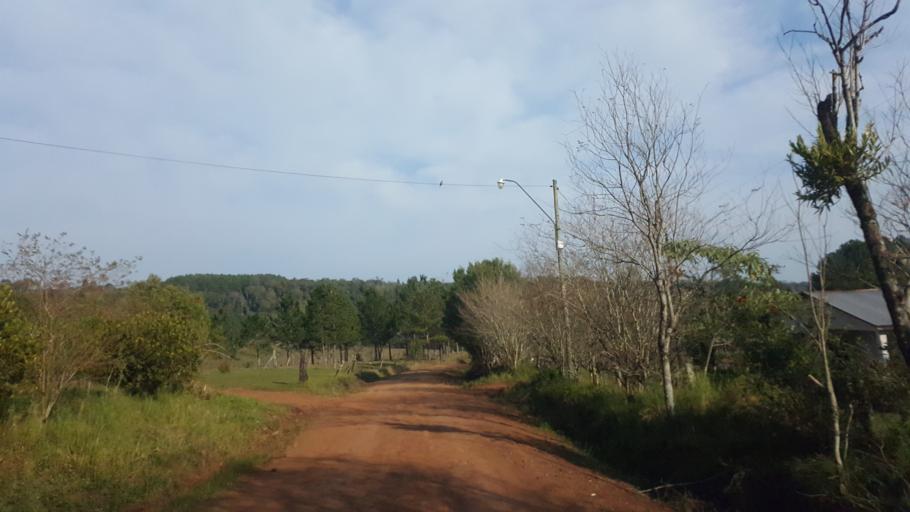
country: AR
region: Misiones
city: Capiovi
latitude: -26.9151
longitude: -55.0807
